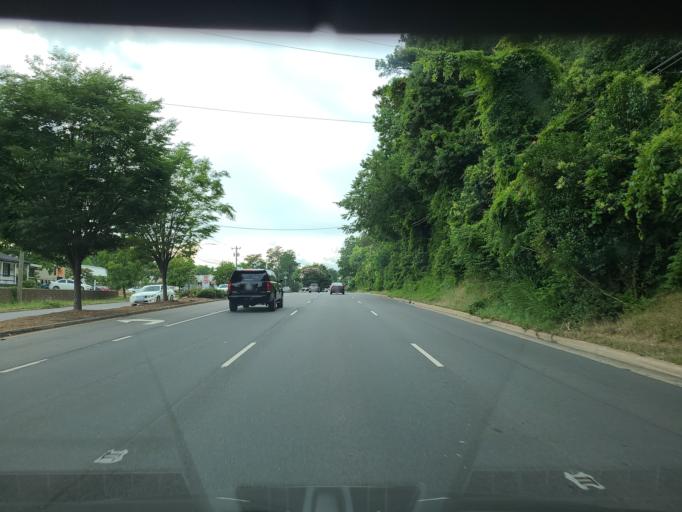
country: US
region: North Carolina
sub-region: Mecklenburg County
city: Charlotte
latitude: 35.2302
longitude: -80.9189
